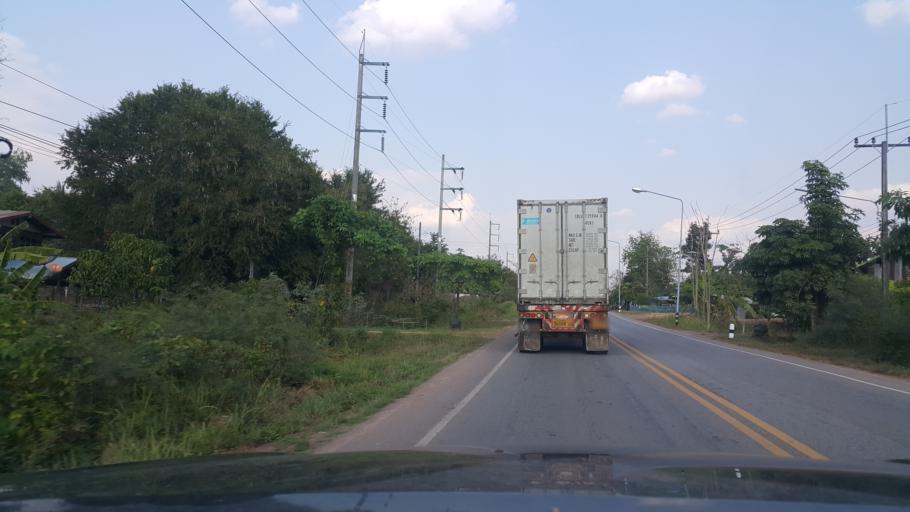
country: TH
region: Phitsanulok
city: Nakhon Thai
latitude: 17.1337
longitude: 100.9288
